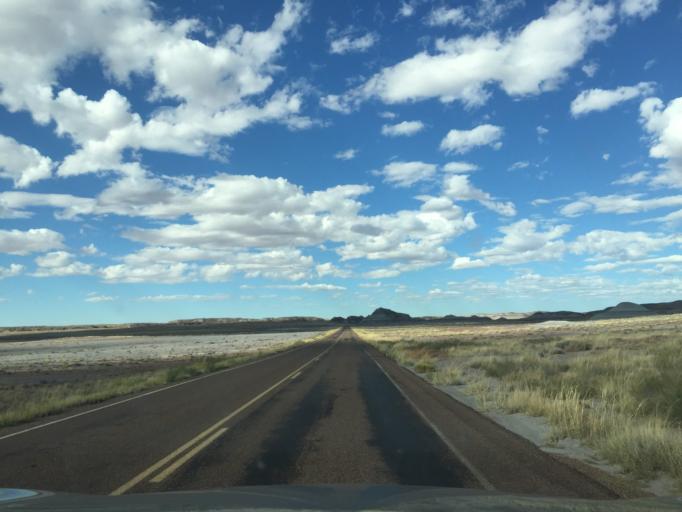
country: US
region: Arizona
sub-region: Navajo County
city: Holbrook
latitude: 34.9324
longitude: -109.7828
